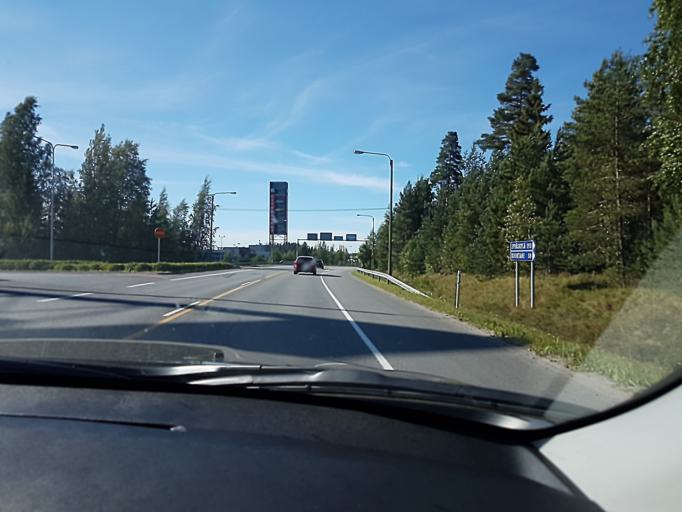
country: FI
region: Southern Ostrobothnia
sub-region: Seinaejoki
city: Nurmo
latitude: 62.7928
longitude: 22.8811
